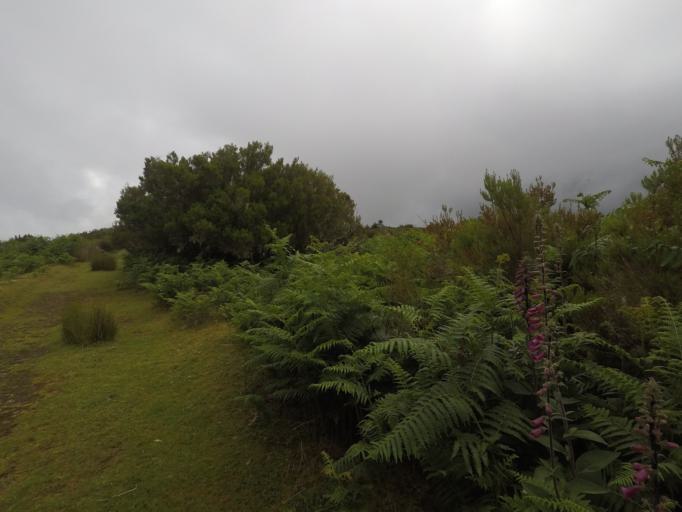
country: PT
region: Madeira
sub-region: Santa Cruz
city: Camacha
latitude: 32.7303
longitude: -16.8848
